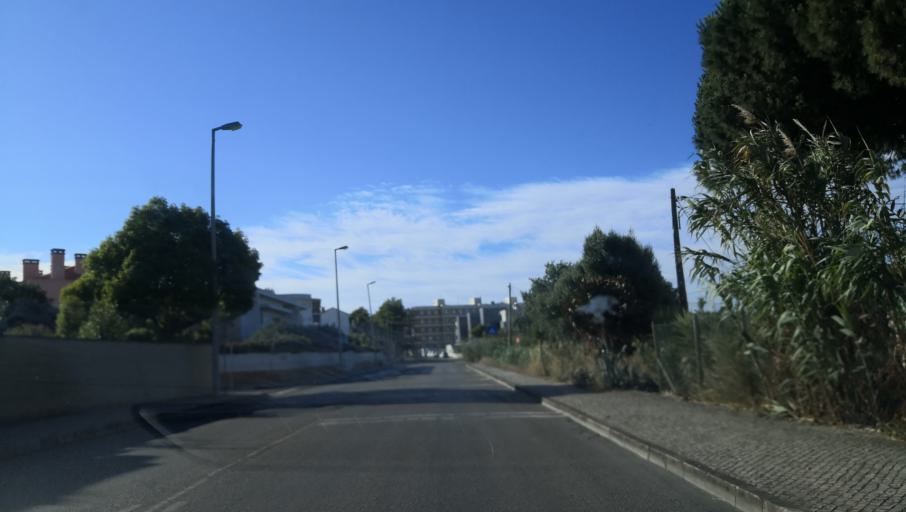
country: PT
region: Lisbon
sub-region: Oeiras
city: Carcavelos
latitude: 38.6842
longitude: -9.3255
